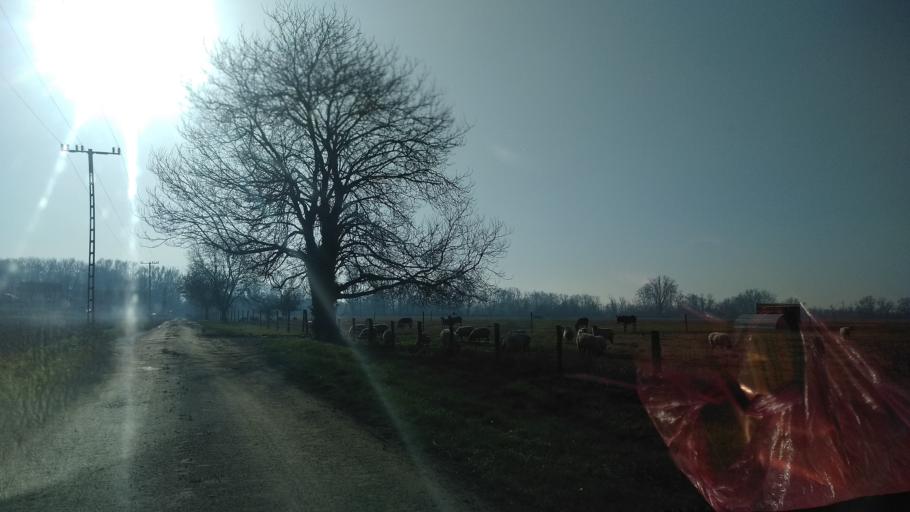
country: HU
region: Somogy
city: Barcs
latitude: 45.9499
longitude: 17.4882
